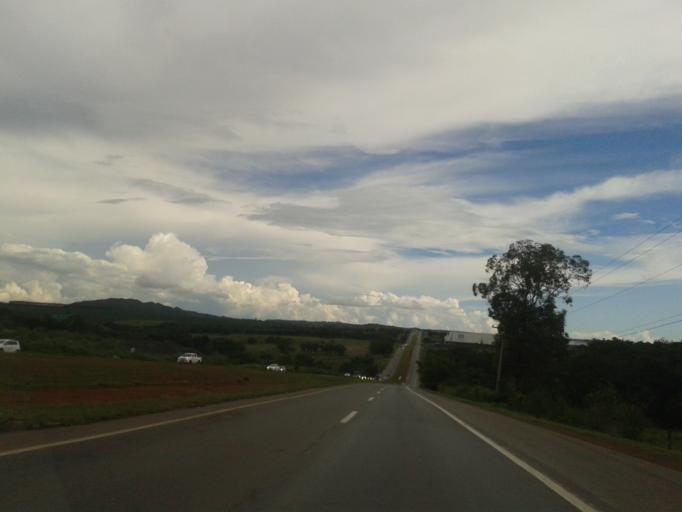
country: BR
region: Goias
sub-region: Aparecida De Goiania
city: Aparecida de Goiania
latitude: -16.8457
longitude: -49.2464
